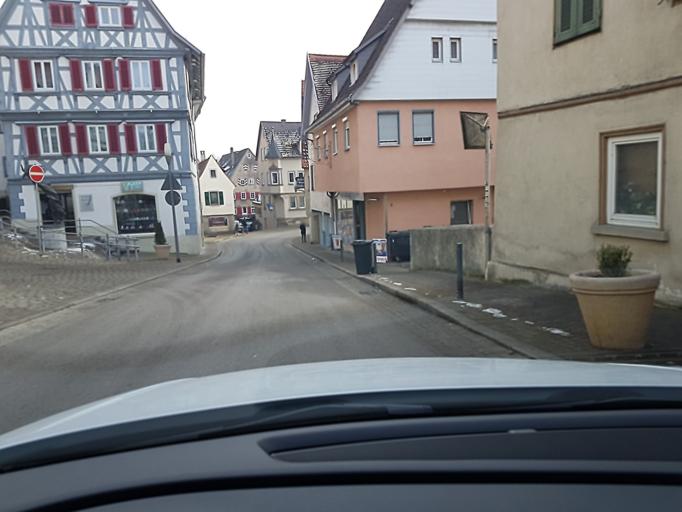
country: DE
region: Baden-Wuerttemberg
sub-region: Regierungsbezirk Stuttgart
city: Besigheim
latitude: 48.9994
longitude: 9.1410
